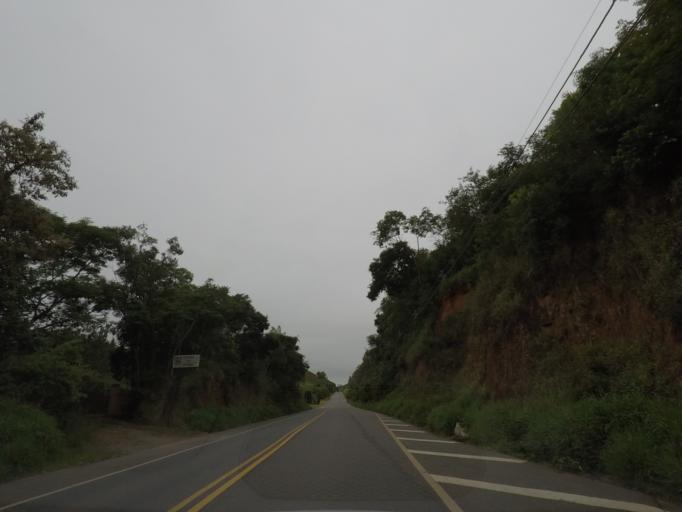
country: BR
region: Sao Paulo
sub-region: Cunha
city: Cunha
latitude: -23.0576
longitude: -44.9882
